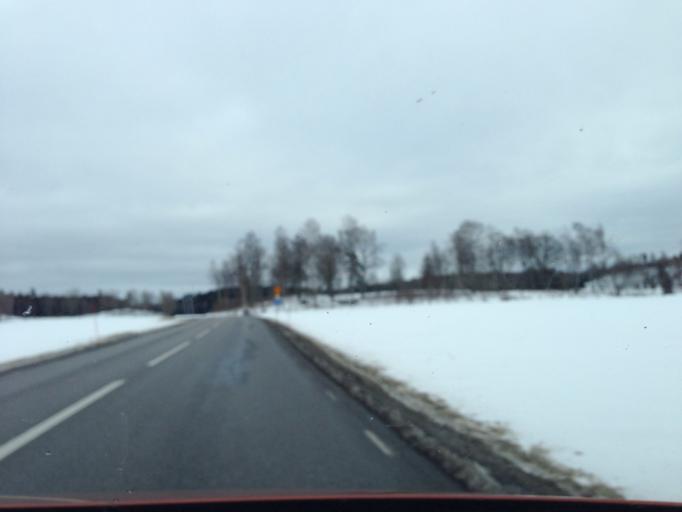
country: SE
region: Stockholm
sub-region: Botkyrka Kommun
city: Varsta
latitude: 59.1224
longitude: 17.8512
